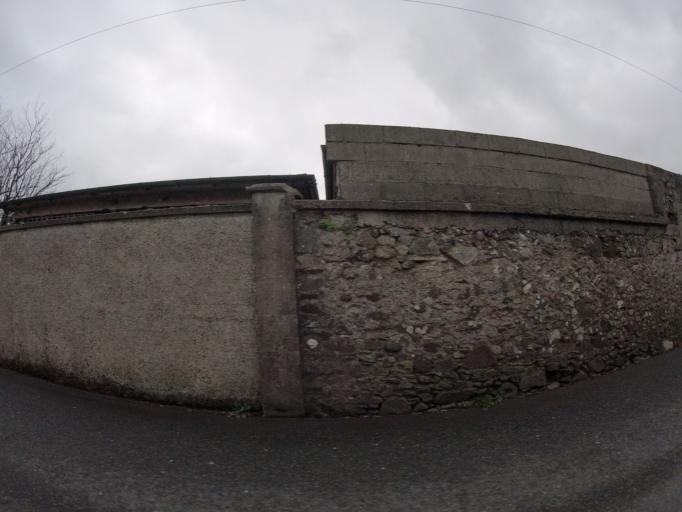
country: IE
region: Munster
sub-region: Waterford
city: Tra Mhor
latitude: 52.1638
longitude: -7.1585
